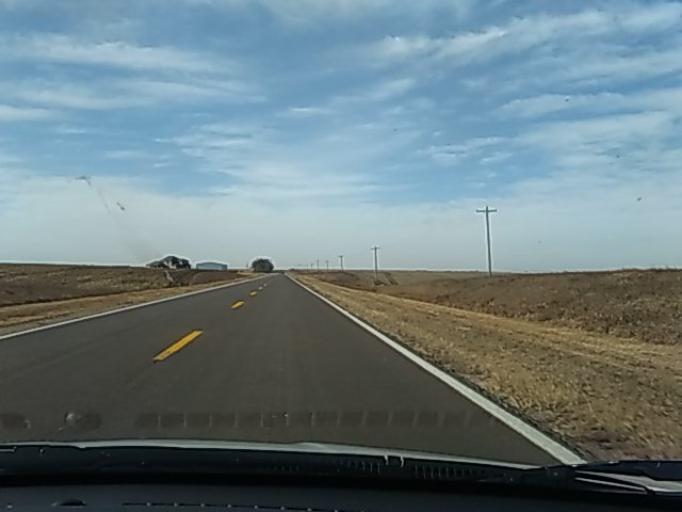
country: US
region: Nebraska
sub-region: Clay County
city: Clay Center
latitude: 40.4233
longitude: -97.9792
